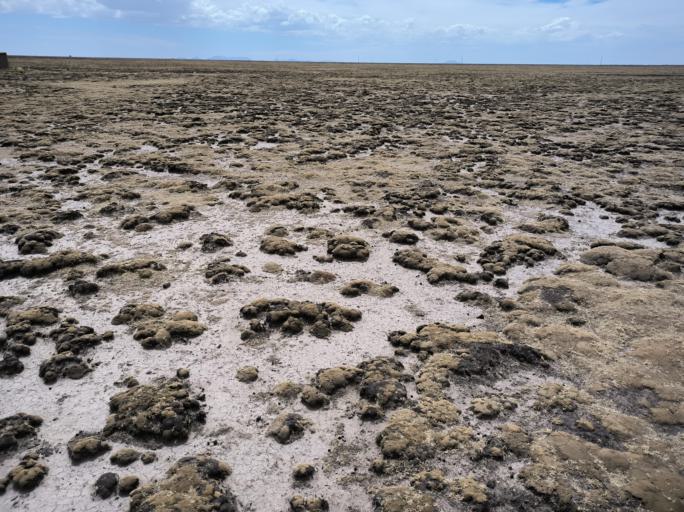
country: BO
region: Oruro
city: Challapata
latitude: -19.1771
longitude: -66.8088
